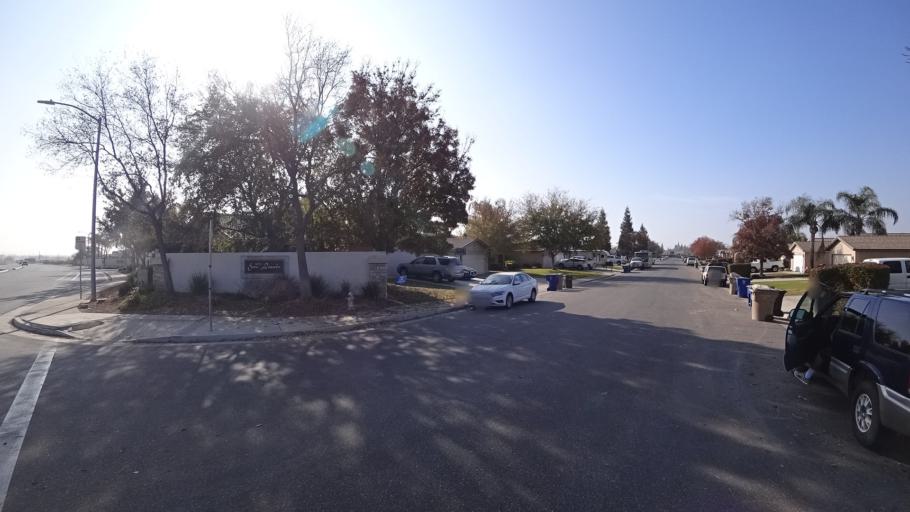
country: US
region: California
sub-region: Kern County
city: Greenacres
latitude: 35.3944
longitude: -119.0661
